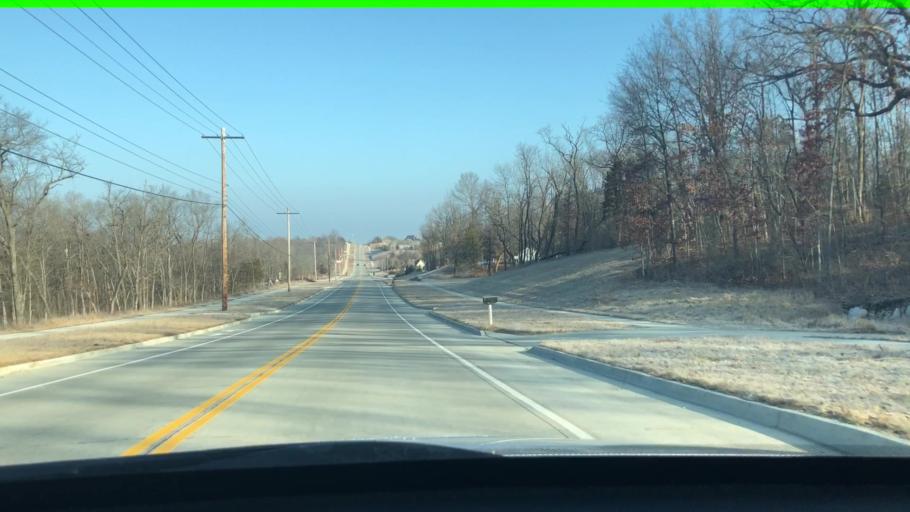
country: US
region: Missouri
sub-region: Boone County
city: Columbia
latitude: 38.9001
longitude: -92.4006
